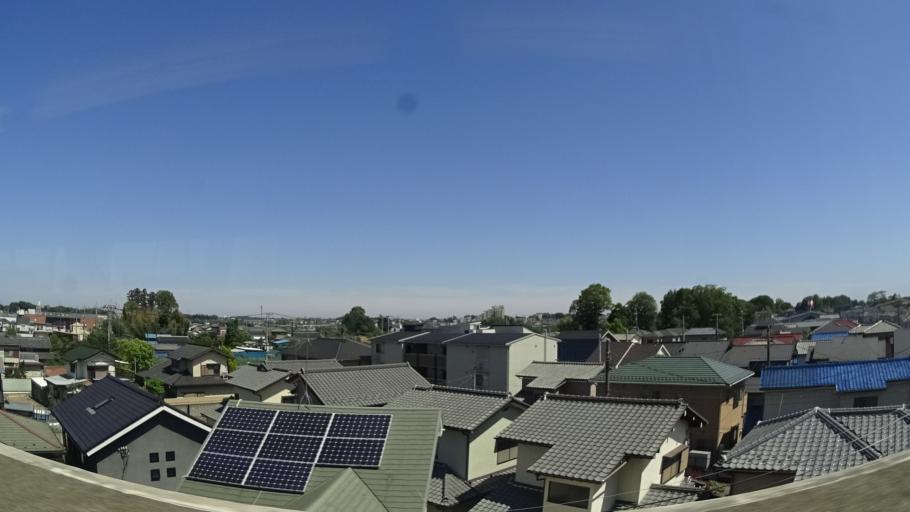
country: JP
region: Saitama
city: Hasuda
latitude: 35.9928
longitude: 139.6337
